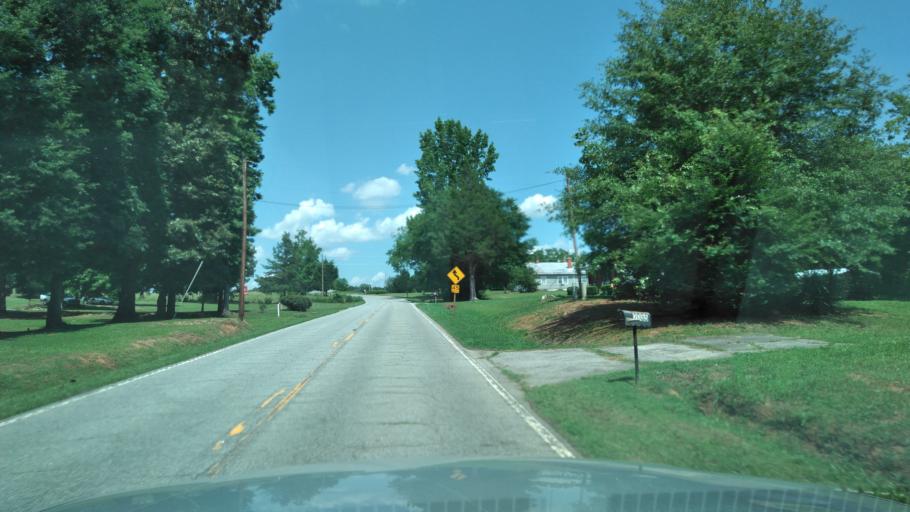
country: US
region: South Carolina
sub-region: Laurens County
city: Laurens
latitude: 34.4938
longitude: -82.1043
